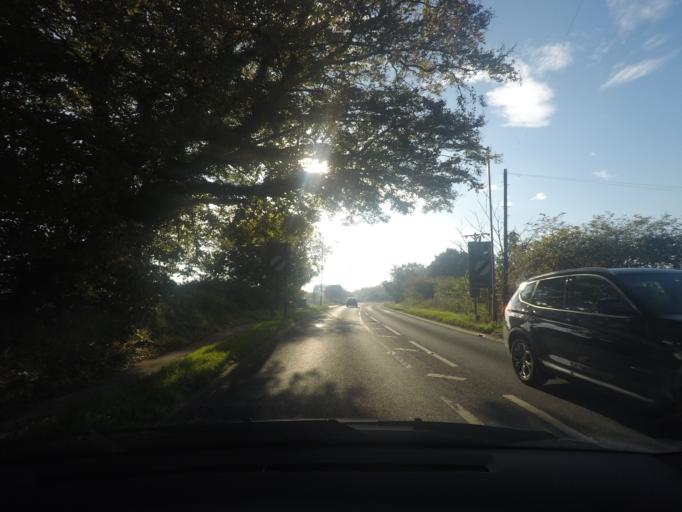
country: GB
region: England
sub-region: East Riding of Yorkshire
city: South Cave
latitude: 53.7642
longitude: -0.6000
